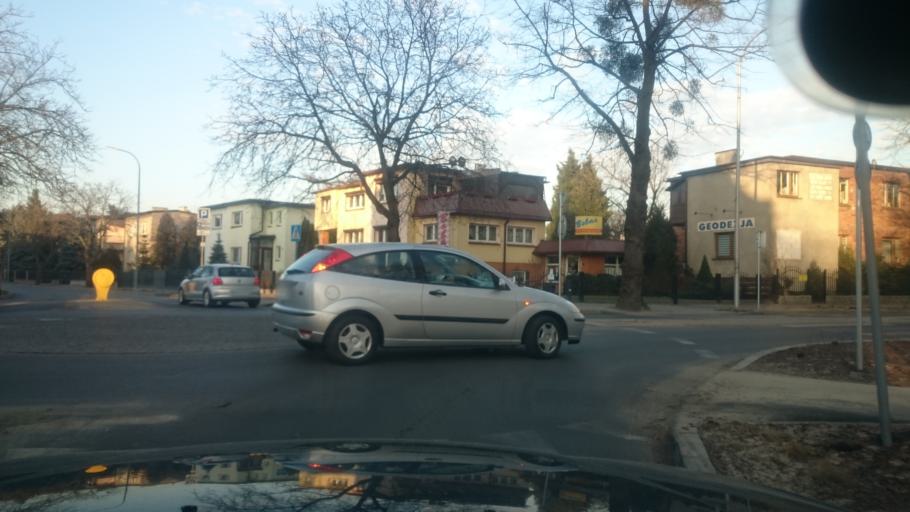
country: PL
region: Greater Poland Voivodeship
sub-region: Powiat ostrowski
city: Ostrow Wielkopolski
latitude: 51.6480
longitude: 17.8215
